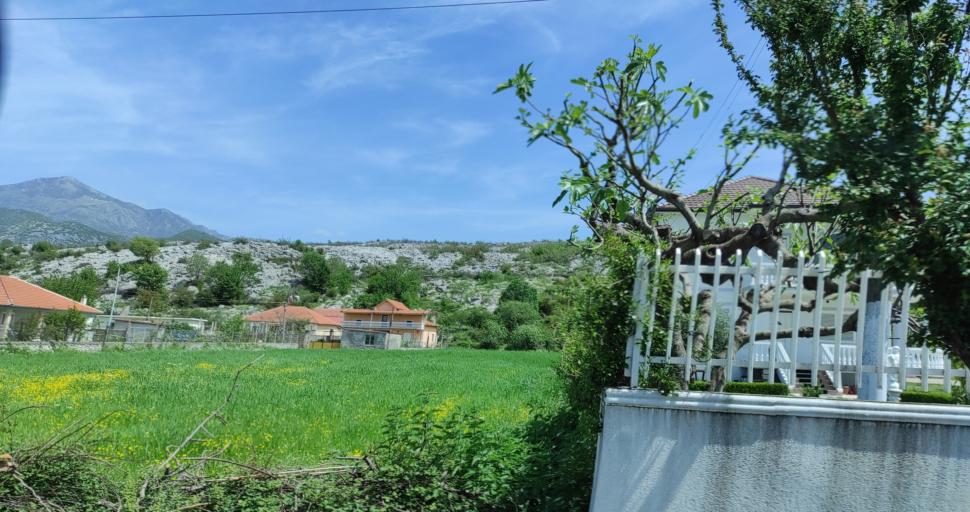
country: AL
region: Shkoder
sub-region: Rrethi i Malesia e Madhe
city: Gruemire
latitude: 42.1252
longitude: 19.5566
